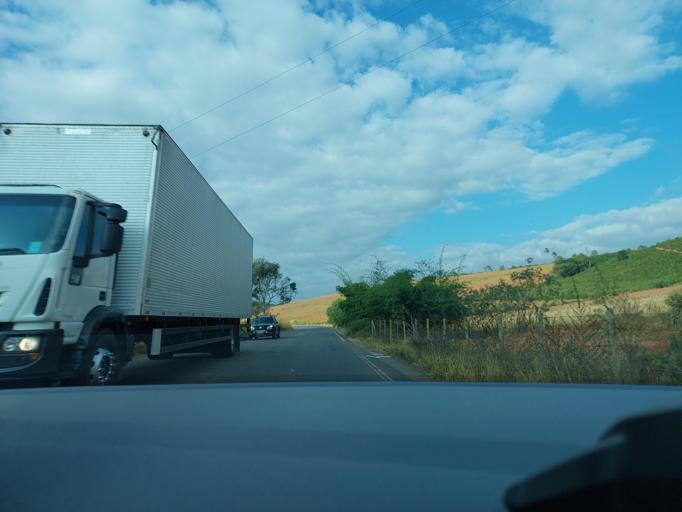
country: BR
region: Minas Gerais
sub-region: Vicosa
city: Vicosa
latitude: -20.8296
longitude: -42.7505
